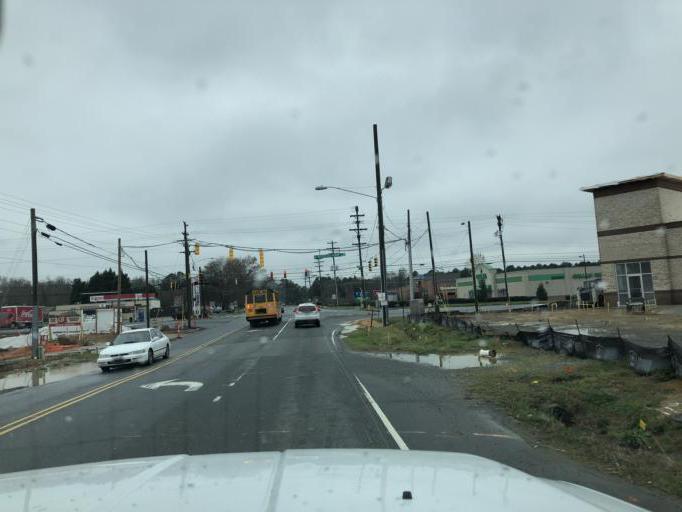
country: US
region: North Carolina
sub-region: Gaston County
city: Mount Holly
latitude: 35.3213
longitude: -80.9520
